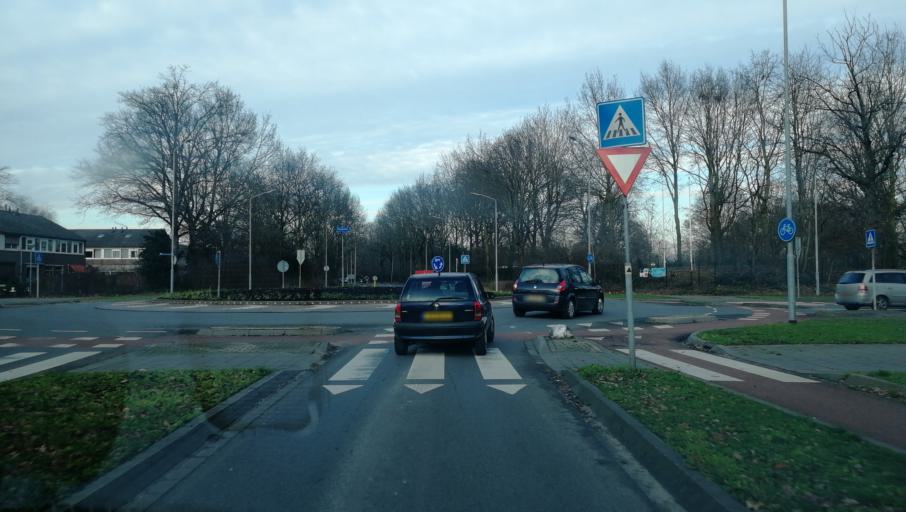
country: NL
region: Limburg
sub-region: Gemeente Venlo
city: Tegelen
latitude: 51.3647
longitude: 6.1347
